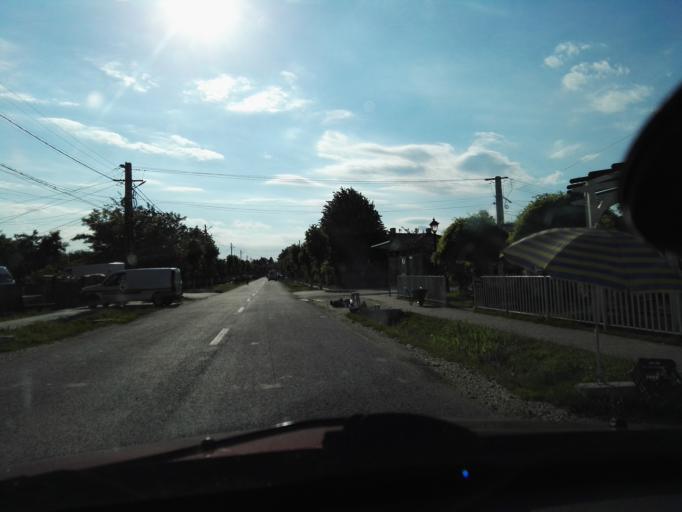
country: RO
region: Giurgiu
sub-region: Comuna Comana
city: Gradistea
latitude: 44.2233
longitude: 26.1494
